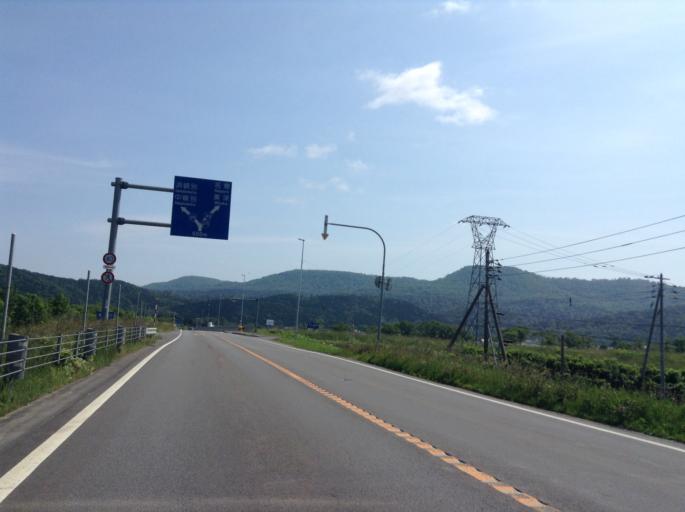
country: JP
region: Hokkaido
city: Nayoro
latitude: 44.7250
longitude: 142.2523
